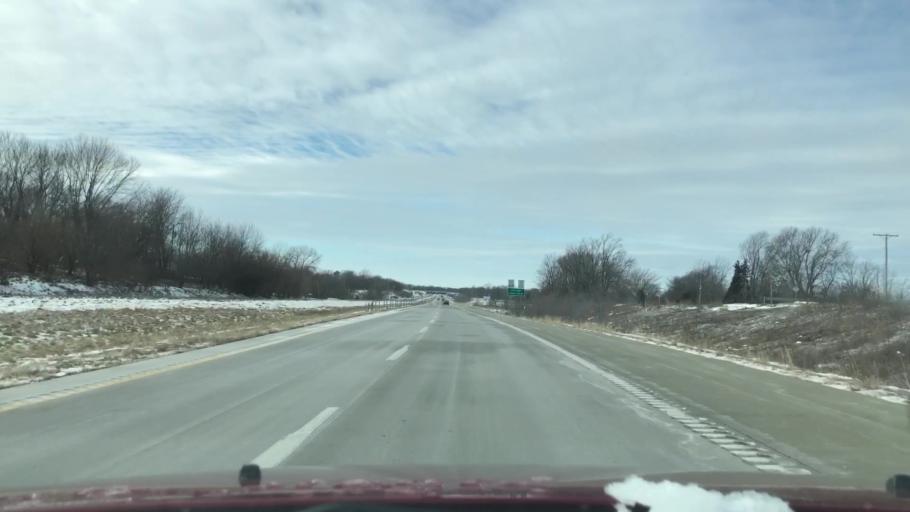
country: US
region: Missouri
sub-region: Jackson County
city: Lone Jack
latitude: 38.8710
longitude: -94.1536
